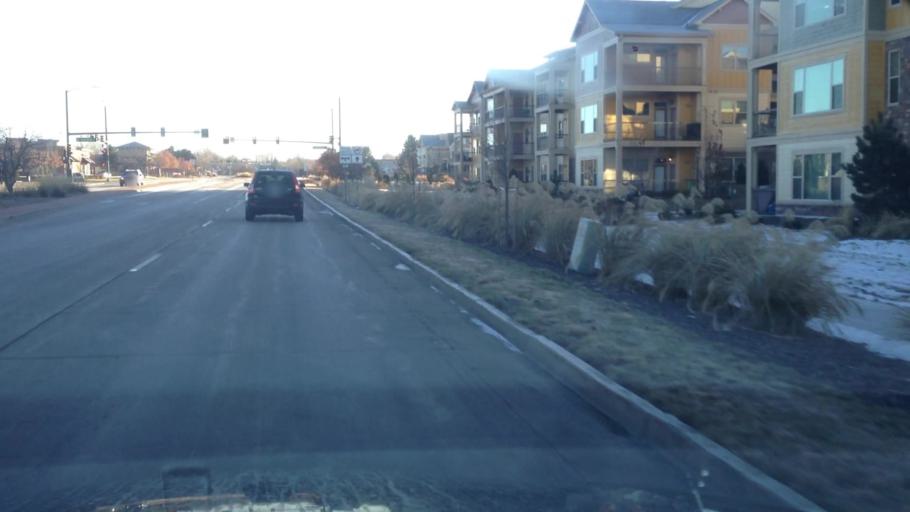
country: US
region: Colorado
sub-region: Douglas County
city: Parker
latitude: 39.5182
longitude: -104.7725
